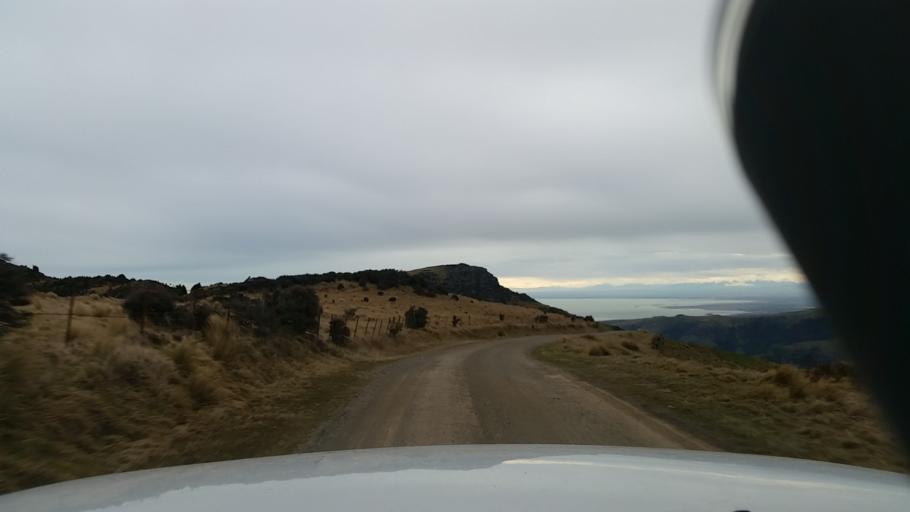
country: NZ
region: Canterbury
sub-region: Christchurch City
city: Christchurch
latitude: -43.8131
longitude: 172.8089
